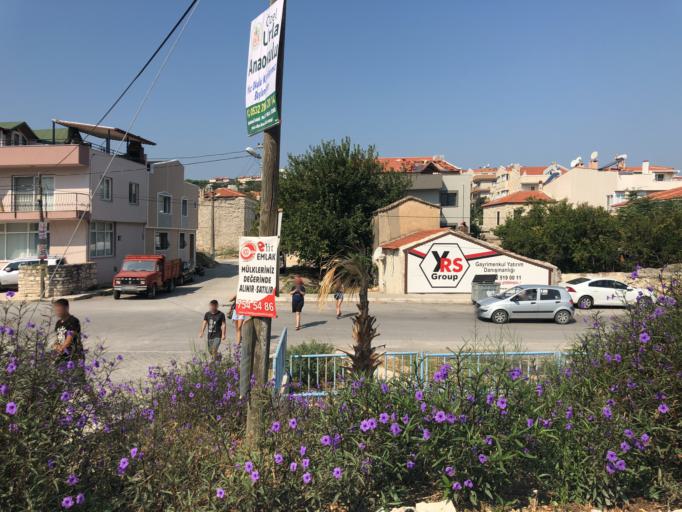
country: TR
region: Izmir
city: Urla
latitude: 38.3269
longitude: 26.7643
